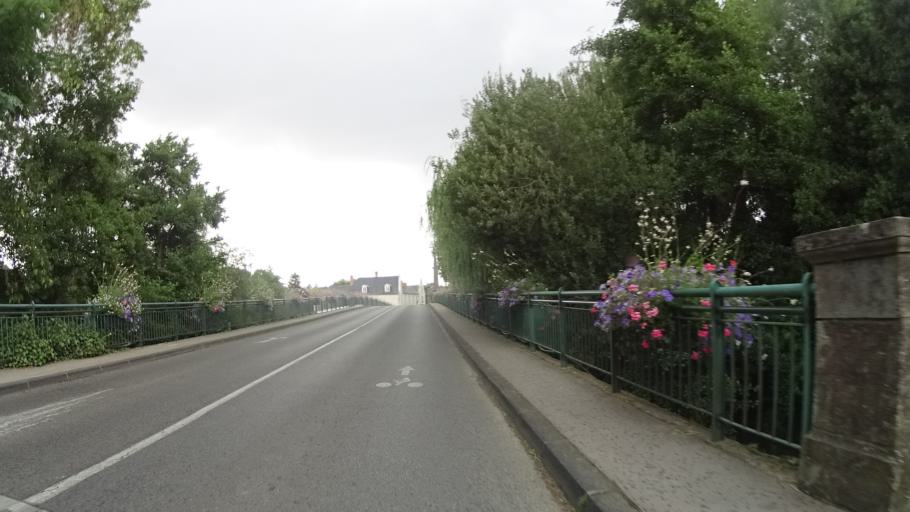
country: FR
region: Centre
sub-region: Departement du Loiret
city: Saint-Hilaire-Saint-Mesmin
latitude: 47.8720
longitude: 1.8400
